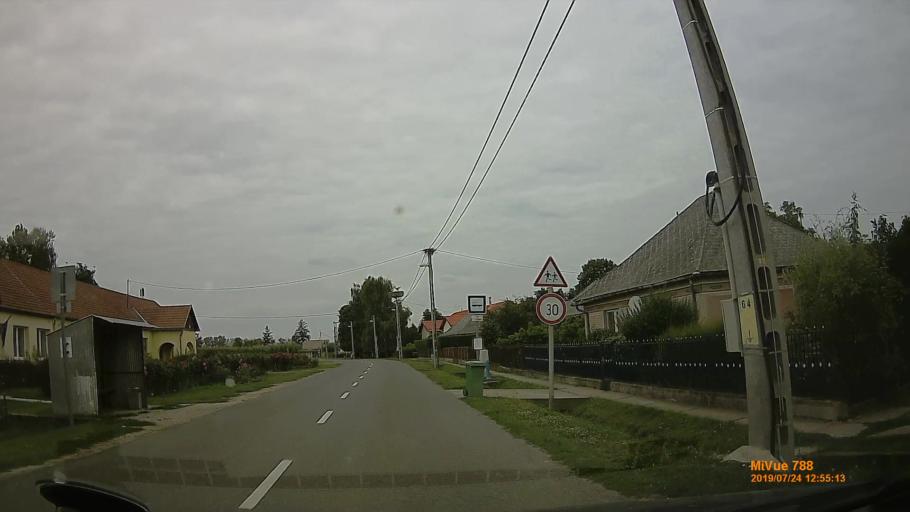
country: HU
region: Szabolcs-Szatmar-Bereg
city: Aranyosapati
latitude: 48.2228
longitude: 22.2929
